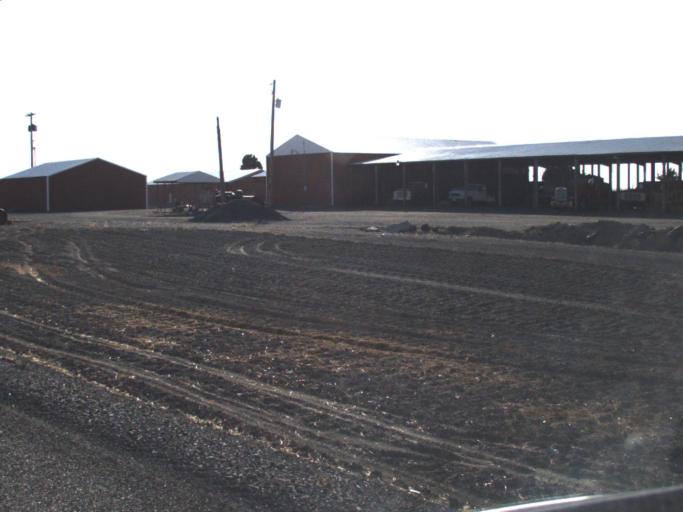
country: US
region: Washington
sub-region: Franklin County
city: Connell
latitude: 46.6634
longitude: -118.8951
